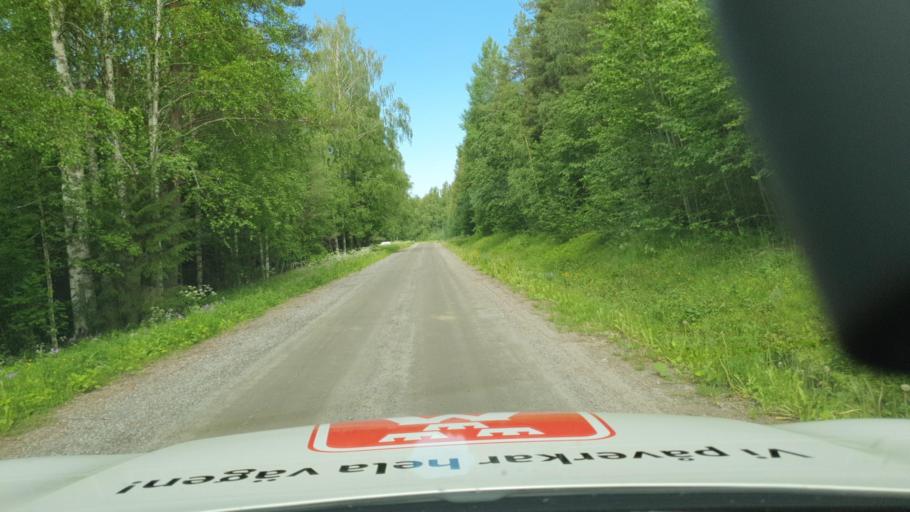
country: SE
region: Vaesterbotten
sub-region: Skelleftea Kommun
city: Forsbacka
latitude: 64.6736
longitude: 20.5300
